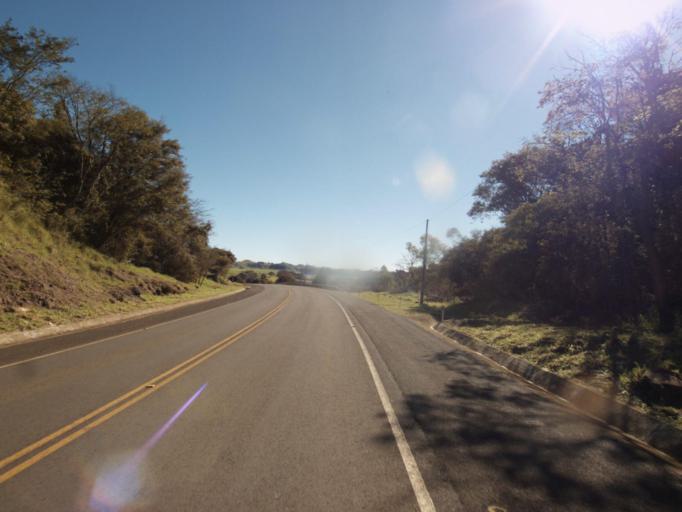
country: AR
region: Misiones
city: Bernardo de Irigoyen
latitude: -26.6403
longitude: -53.6271
